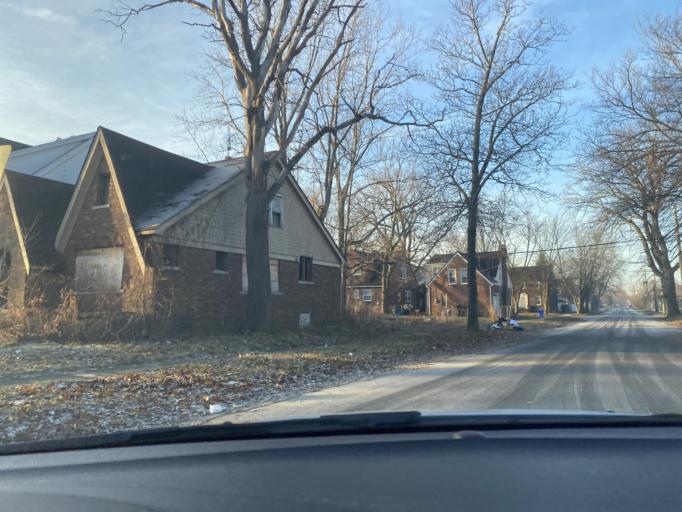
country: US
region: Michigan
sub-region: Wayne County
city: Grosse Pointe Park
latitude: 42.4046
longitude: -82.9451
